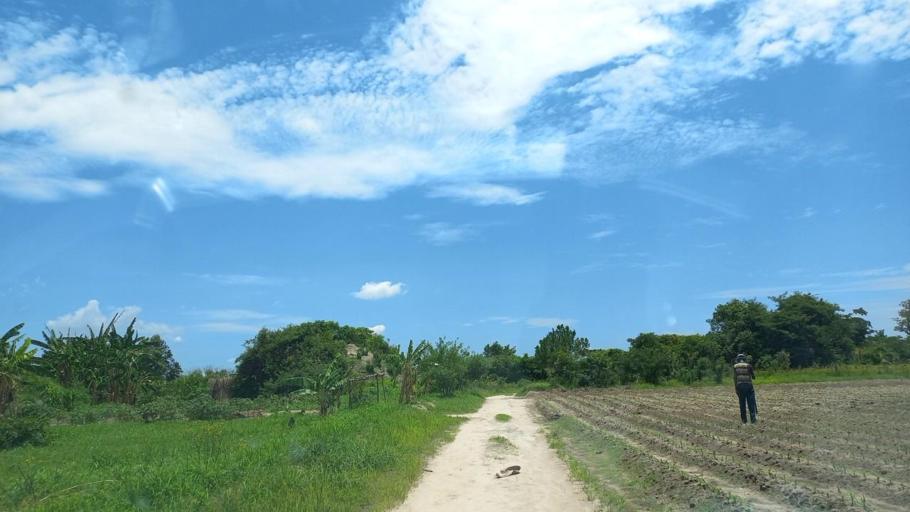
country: ZM
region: Copperbelt
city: Ndola
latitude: -12.8679
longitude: 28.4396
